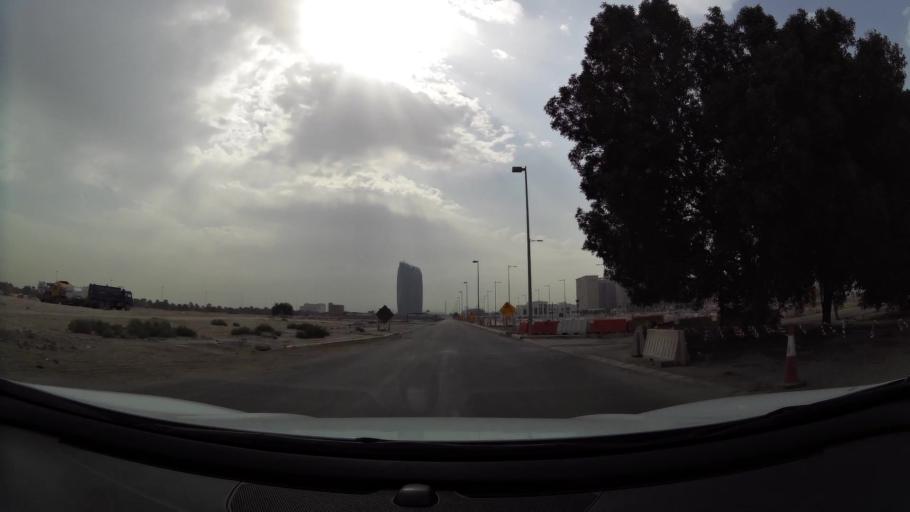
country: AE
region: Abu Dhabi
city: Abu Dhabi
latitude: 24.4633
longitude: 54.3923
